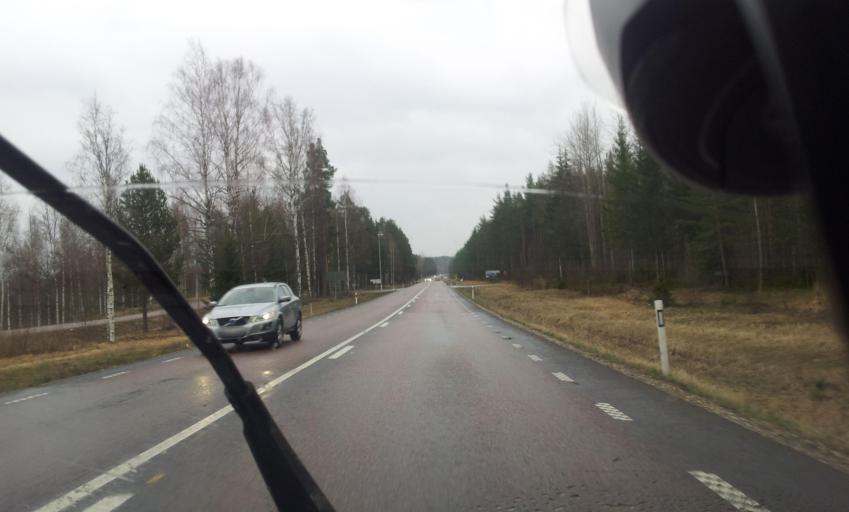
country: SE
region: Dalarna
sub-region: Borlange Kommun
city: Borlaenge
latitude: 60.5244
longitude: 15.3544
